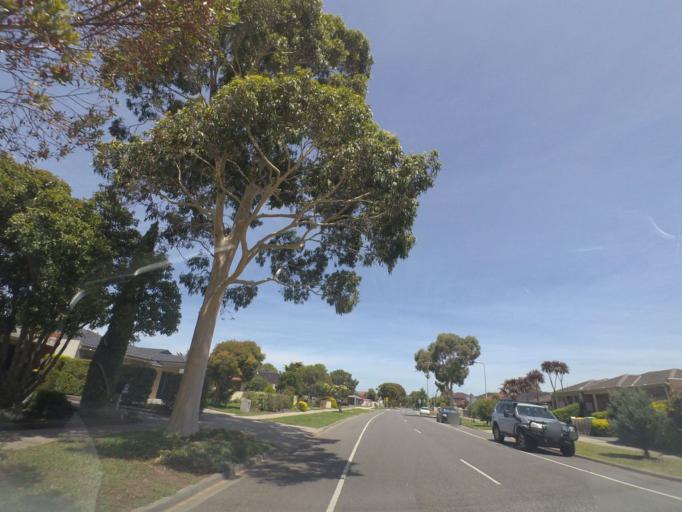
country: AU
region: Victoria
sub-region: Brimbank
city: Keilor Downs
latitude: -37.7201
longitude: 144.8126
